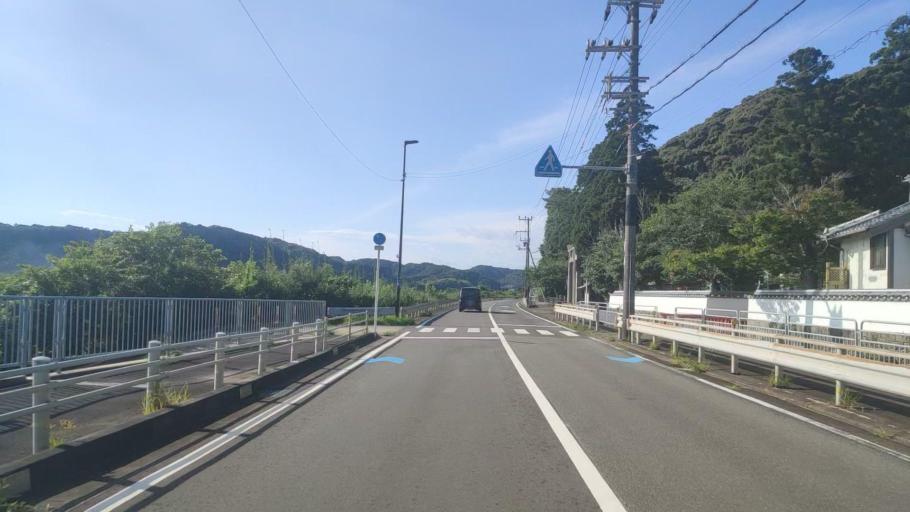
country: JP
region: Wakayama
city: Tanabe
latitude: 33.6545
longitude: 135.4023
